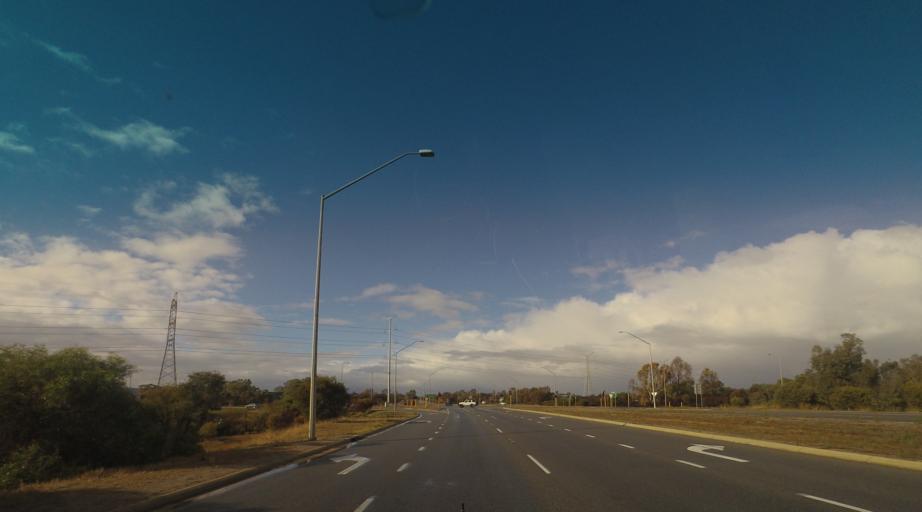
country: AU
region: Western Australia
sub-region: Armadale
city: Seville Grove
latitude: -32.1466
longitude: 115.9566
